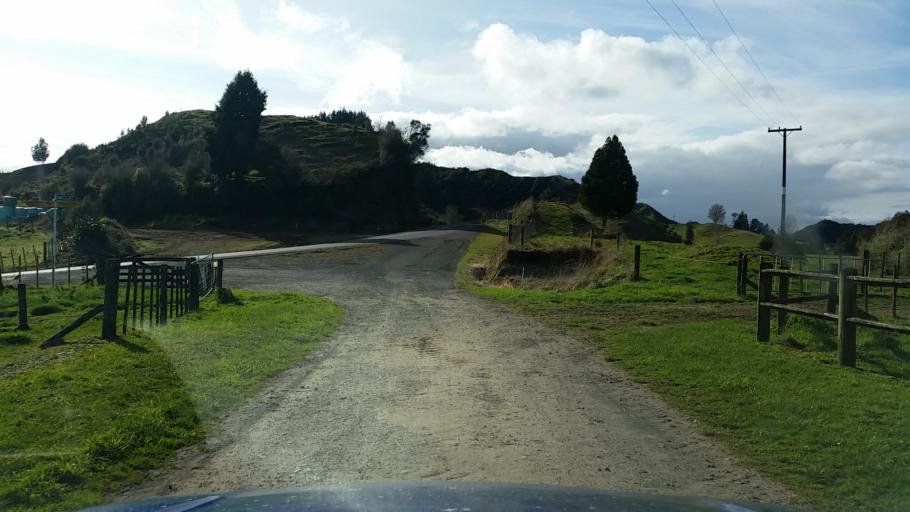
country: NZ
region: Taranaki
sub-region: South Taranaki District
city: Eltham
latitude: -39.2565
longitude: 174.5742
